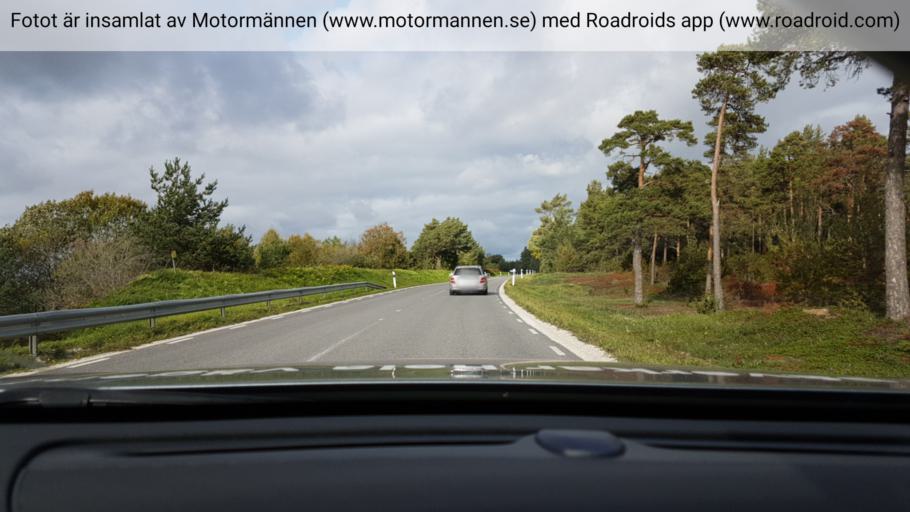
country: SE
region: Gotland
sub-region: Gotland
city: Vibble
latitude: 57.5842
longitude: 18.2965
